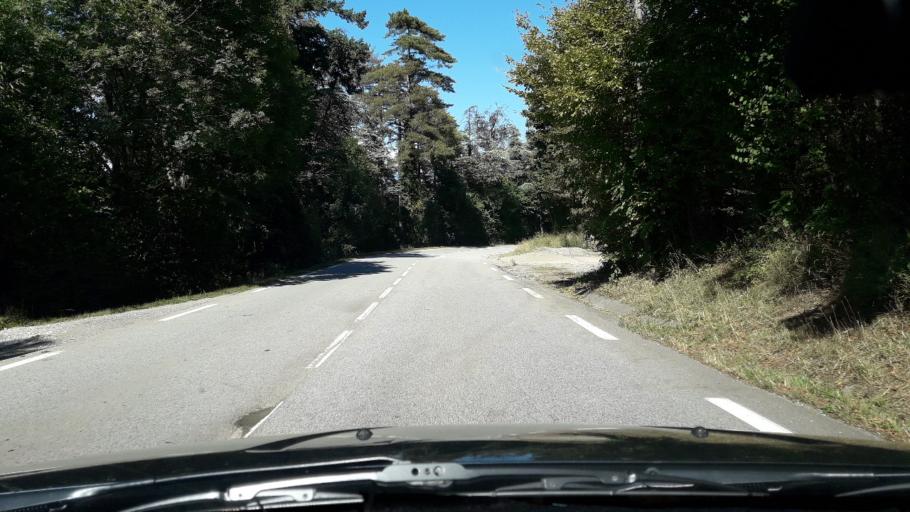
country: FR
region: Rhone-Alpes
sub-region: Departement de l'Isere
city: Vif
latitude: 45.0344
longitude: 5.6659
